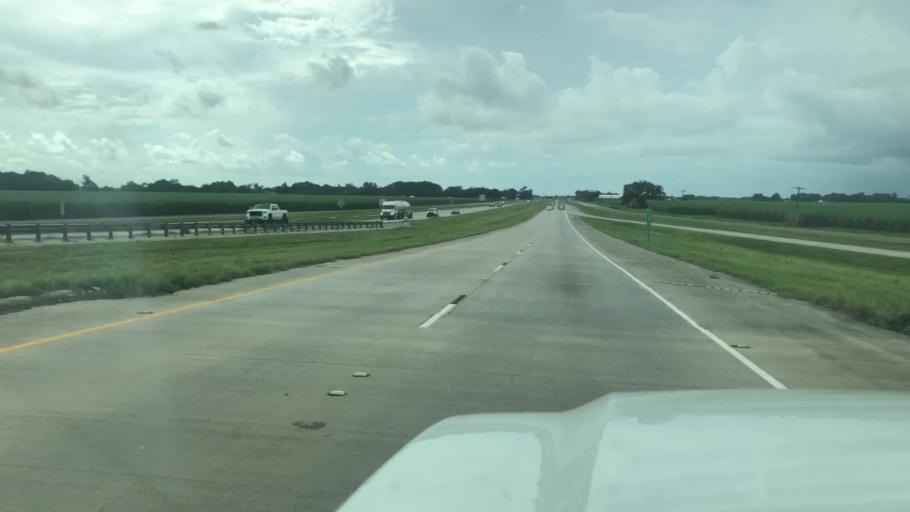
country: US
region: Louisiana
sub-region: Iberia Parish
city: Jeanerette
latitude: 29.9210
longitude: -91.7304
